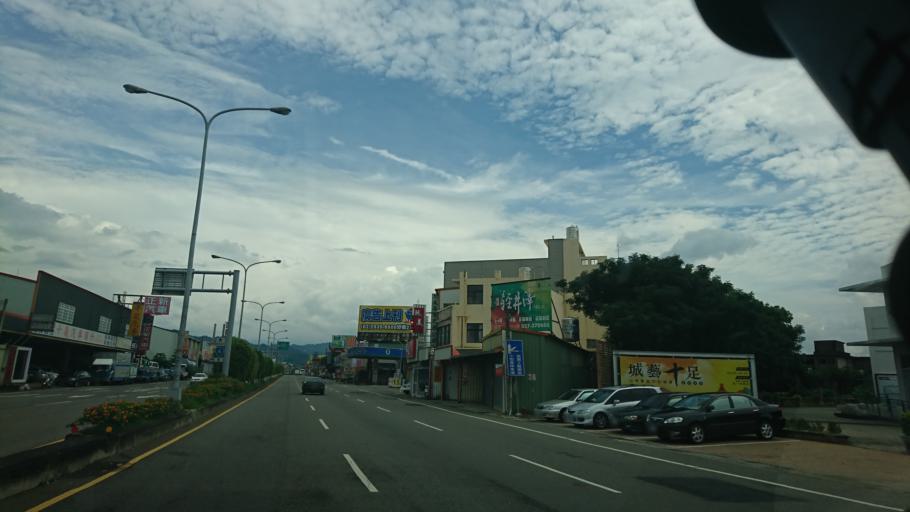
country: TW
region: Taiwan
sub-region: Miaoli
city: Miaoli
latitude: 24.5334
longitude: 120.8170
